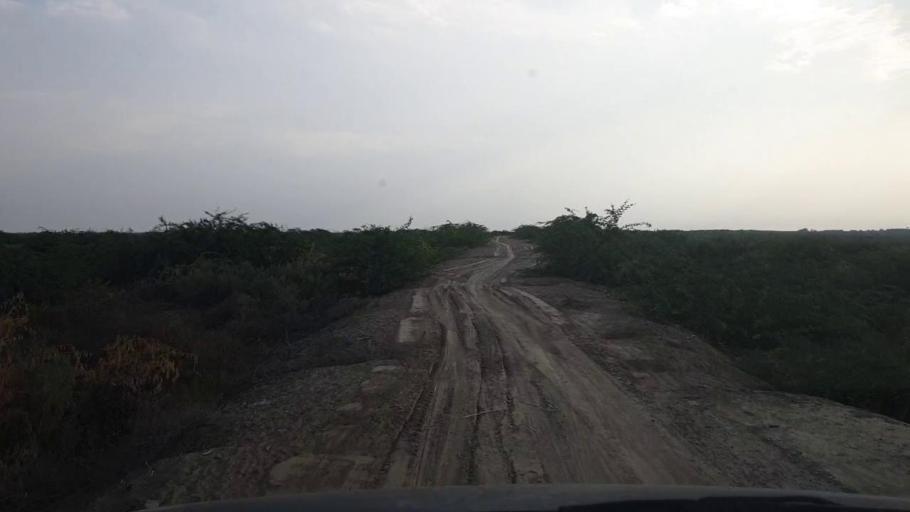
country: PK
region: Sindh
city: Badin
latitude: 24.4764
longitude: 68.7000
